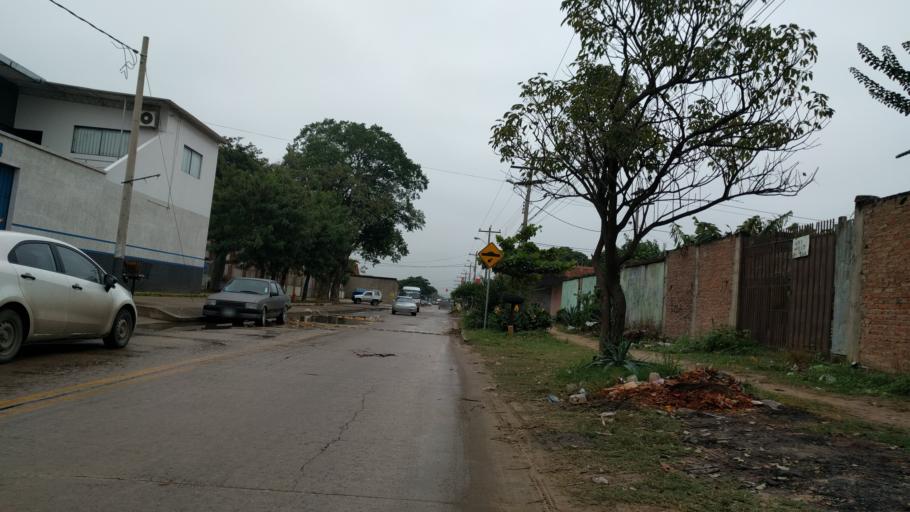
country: BO
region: Santa Cruz
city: Santa Cruz de la Sierra
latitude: -17.8215
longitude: -63.1663
